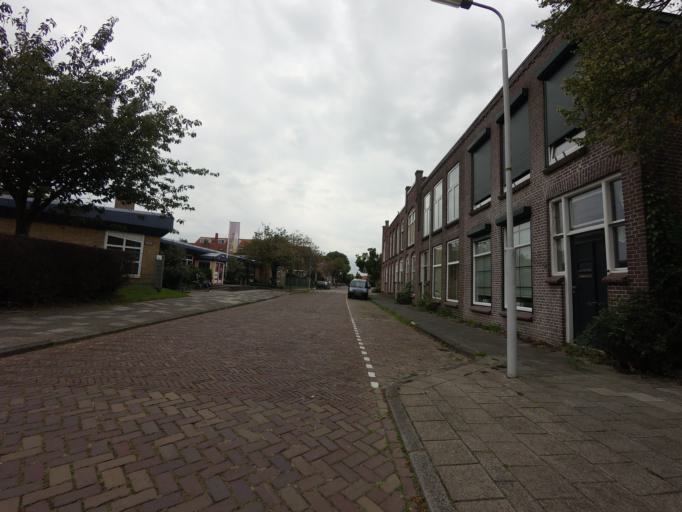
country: NL
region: Friesland
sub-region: Sudwest Fryslan
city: Sneek
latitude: 53.0350
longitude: 5.6602
